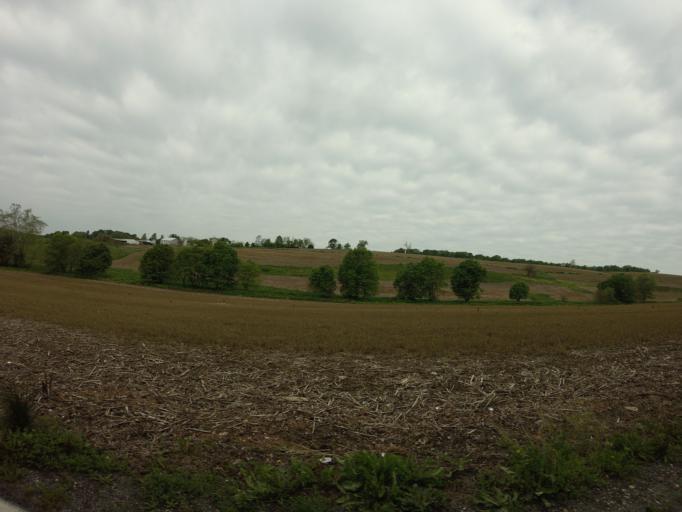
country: US
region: Maryland
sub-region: Montgomery County
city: Damascus
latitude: 39.3121
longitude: -77.2385
